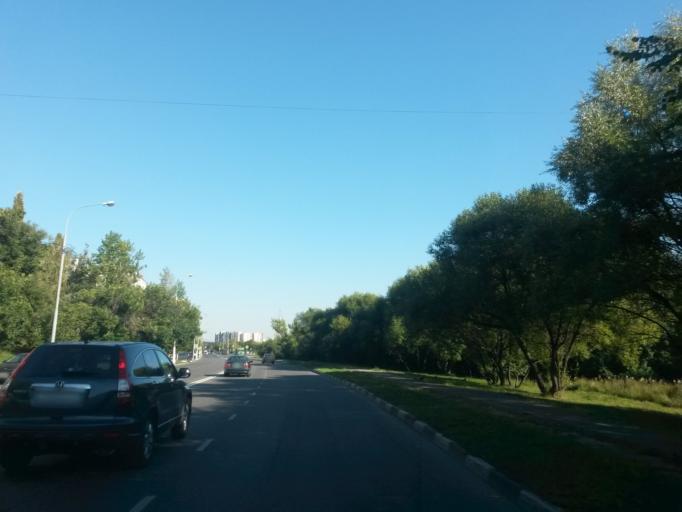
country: RU
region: Moscow
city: Yasenevo
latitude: 55.6015
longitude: 37.5152
